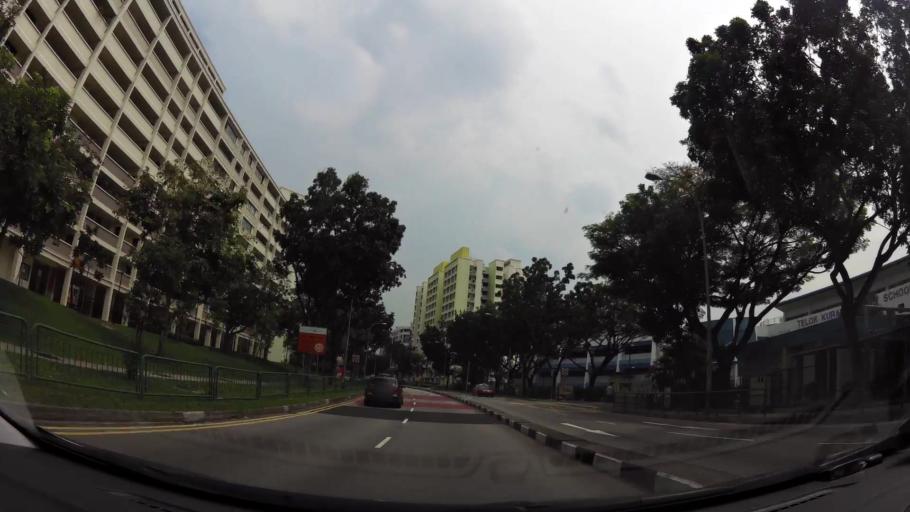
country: SG
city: Singapore
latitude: 1.3317
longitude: 103.9105
